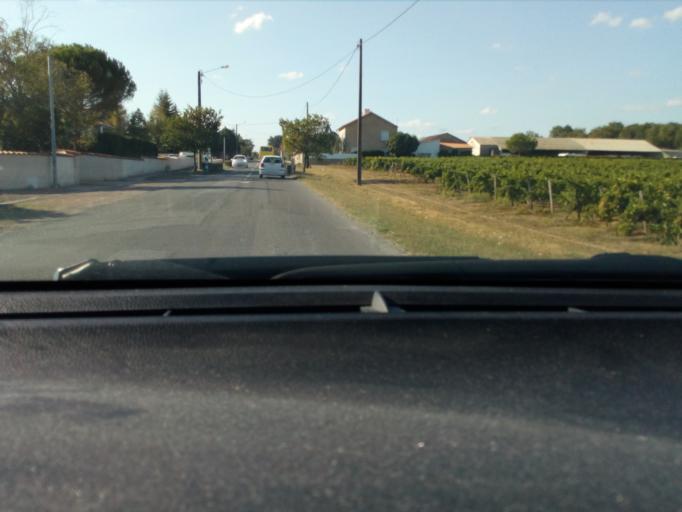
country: FR
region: Poitou-Charentes
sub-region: Departement de la Charente
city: Saint-Yrieix-sur-Charente
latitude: 45.6805
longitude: 0.1168
